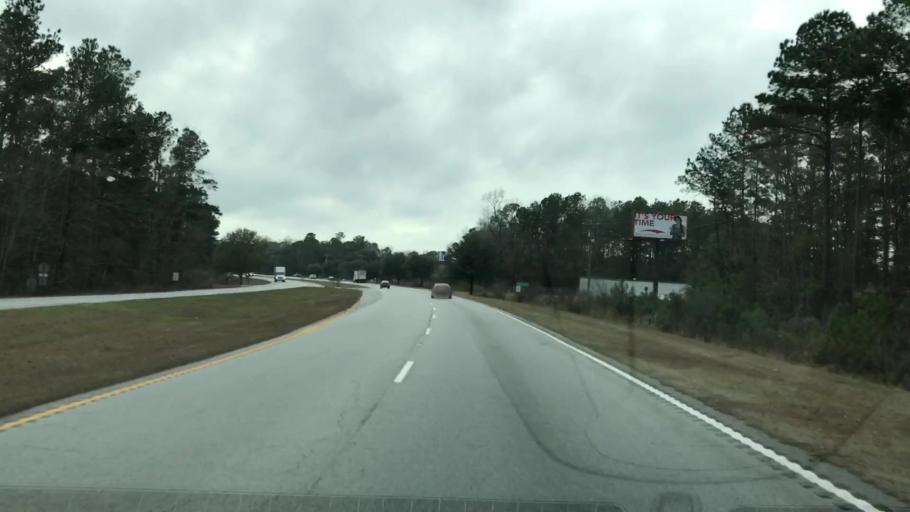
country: US
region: South Carolina
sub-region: Berkeley County
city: Moncks Corner
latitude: 33.1847
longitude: -80.0126
